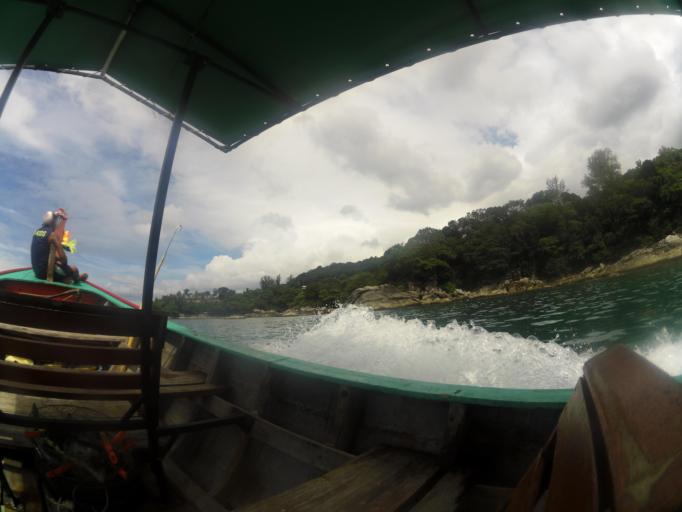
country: TH
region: Phuket
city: Patong
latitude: 7.9648
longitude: 98.2786
